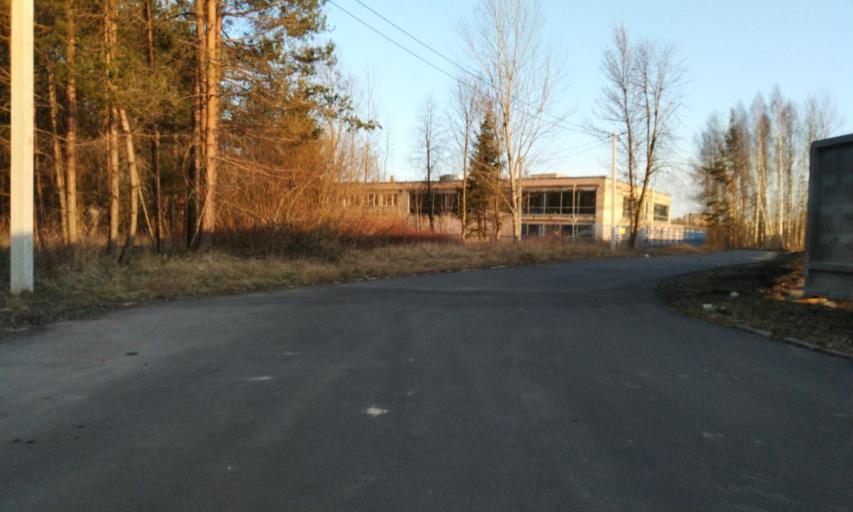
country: RU
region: Leningrad
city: Novoye Devyatkino
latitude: 60.0757
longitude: 30.4690
